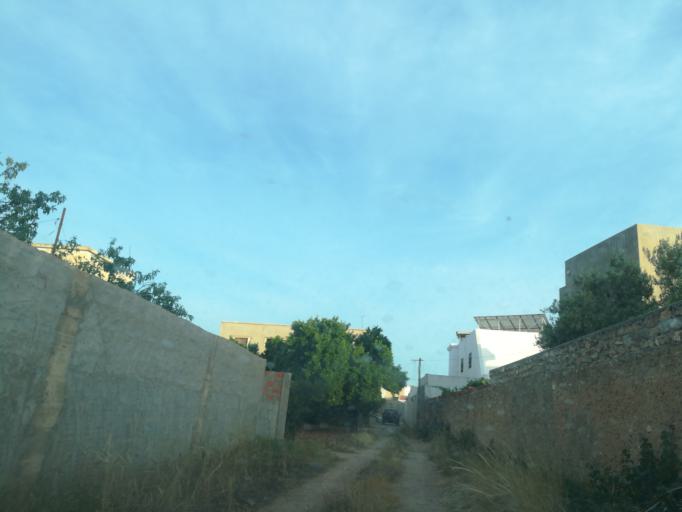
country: TN
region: Safaqis
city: Al Qarmadah
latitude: 34.8221
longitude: 10.7575
